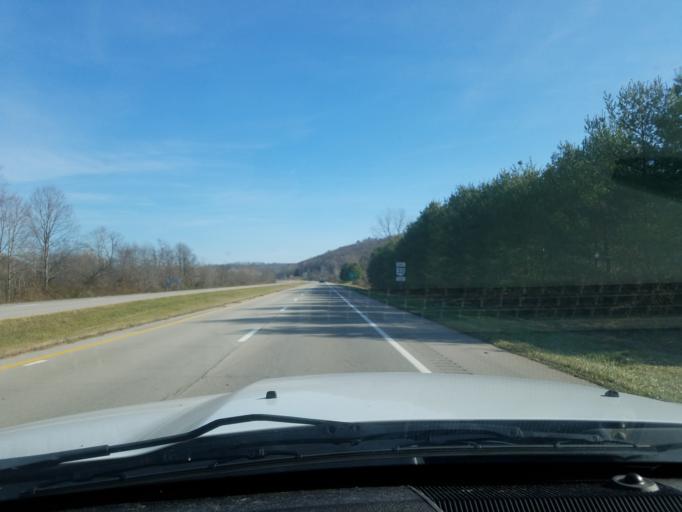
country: US
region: Ohio
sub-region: Pike County
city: Piketon
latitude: 39.0425
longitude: -83.1560
